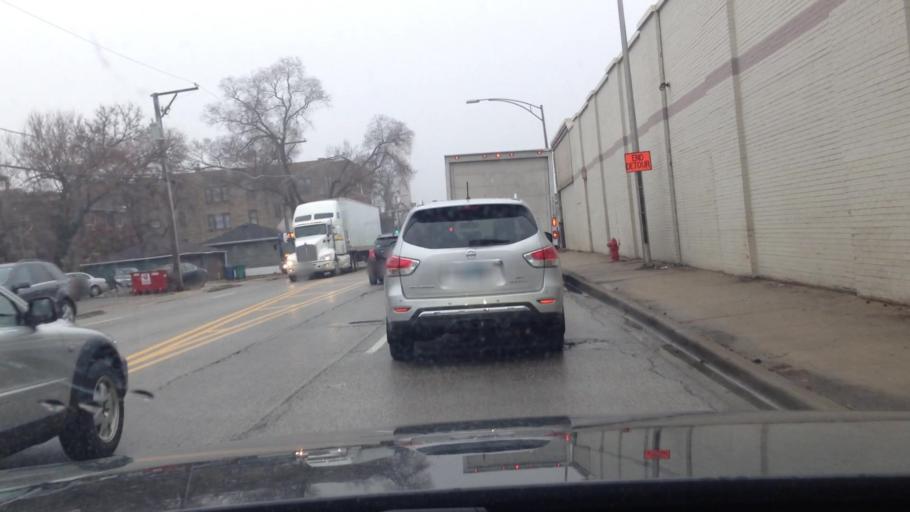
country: US
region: Illinois
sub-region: Cook County
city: Forest Park
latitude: 41.8828
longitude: -87.8049
